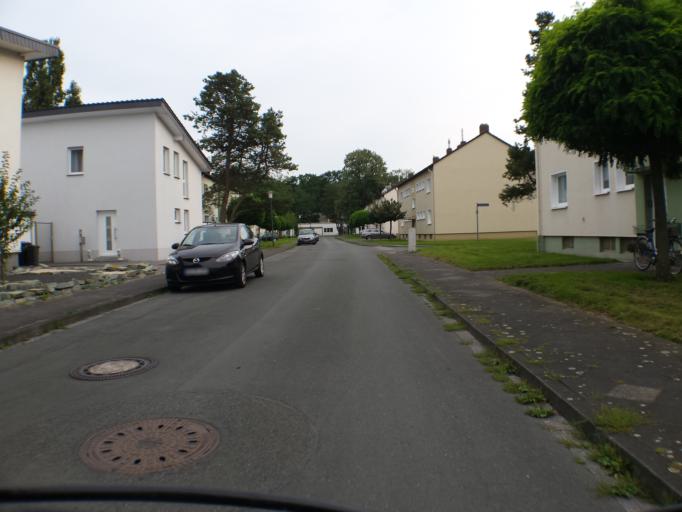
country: DE
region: North Rhine-Westphalia
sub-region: Regierungsbezirk Arnsberg
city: Lippstadt
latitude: 51.6823
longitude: 8.3240
